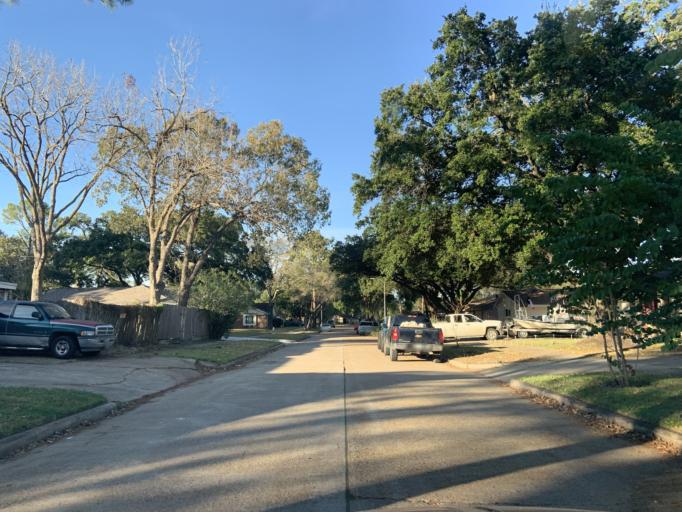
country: US
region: Texas
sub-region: Harris County
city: Bellaire
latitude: 29.6858
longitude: -95.5159
